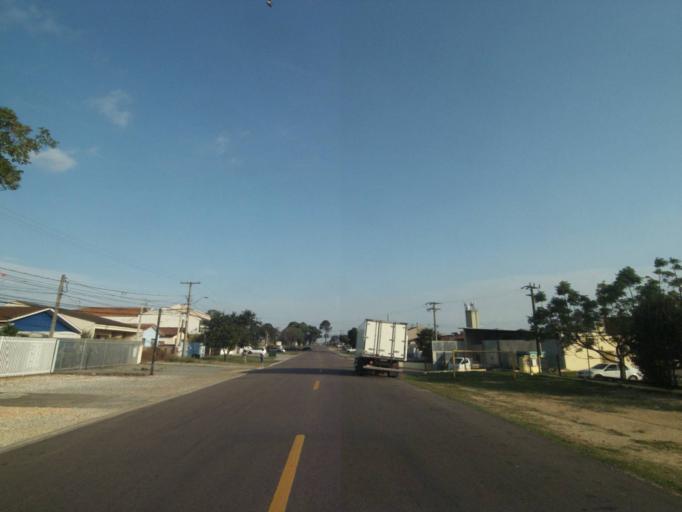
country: BR
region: Parana
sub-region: Curitiba
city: Curitiba
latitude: -25.4862
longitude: -49.3249
